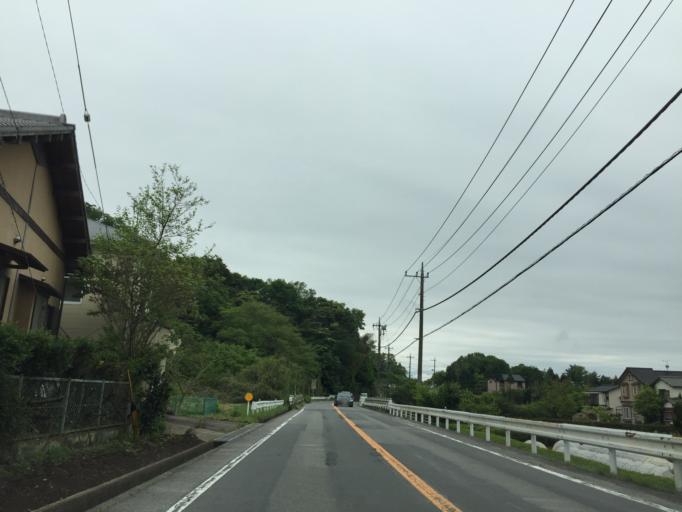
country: JP
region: Shizuoka
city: Mishima
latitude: 35.1782
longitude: 138.9202
